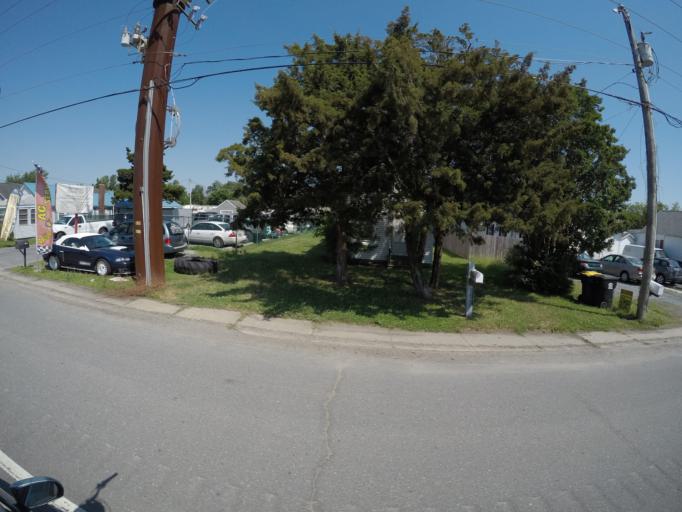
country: US
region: Delaware
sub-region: Sussex County
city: Lewes
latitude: 38.7460
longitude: -75.1807
